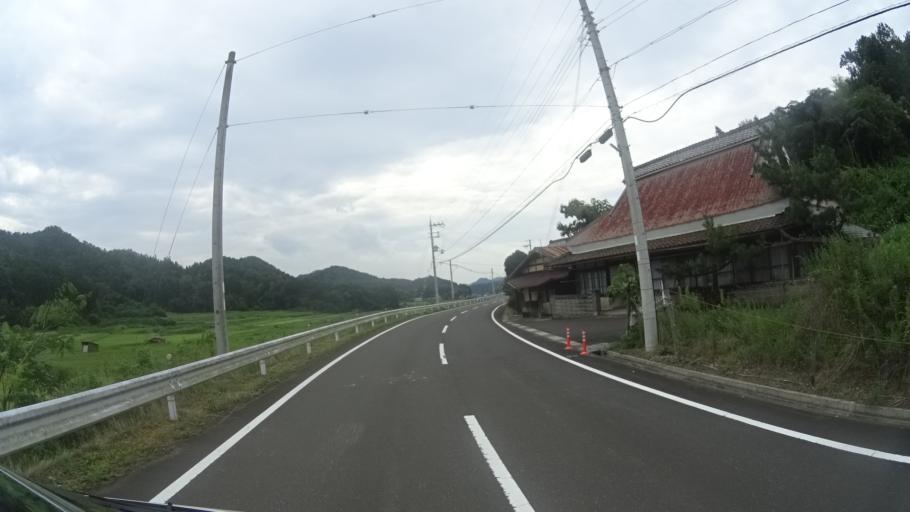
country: JP
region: Kyoto
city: Maizuru
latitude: 35.3556
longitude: 135.3310
